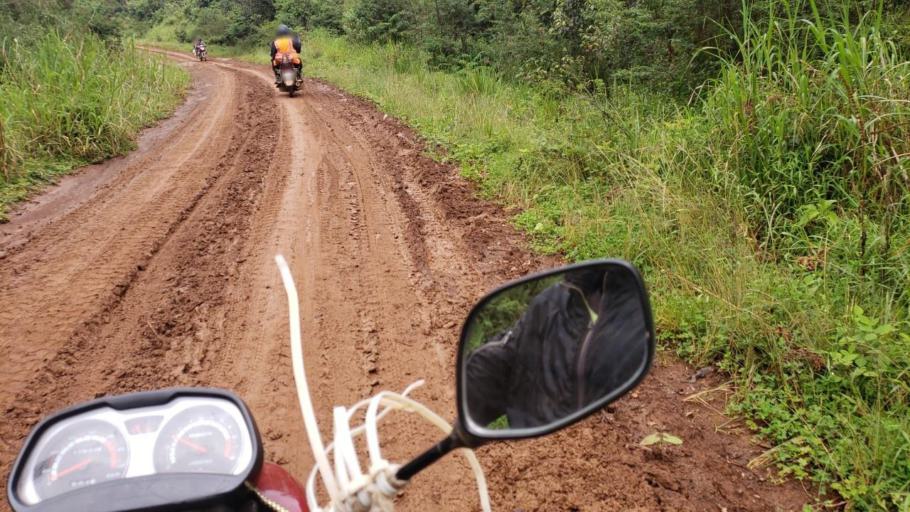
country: CD
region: South Kivu
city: Kabare
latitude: -2.2681
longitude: 28.6622
